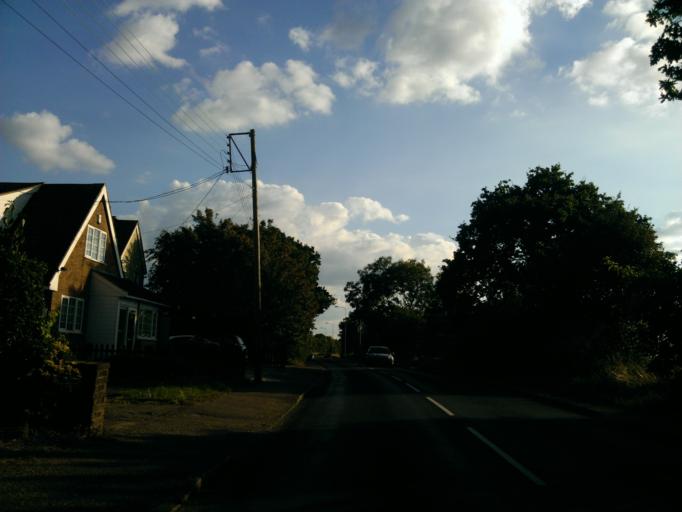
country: GB
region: England
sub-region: Essex
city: Braintree
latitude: 51.9019
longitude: 0.5707
